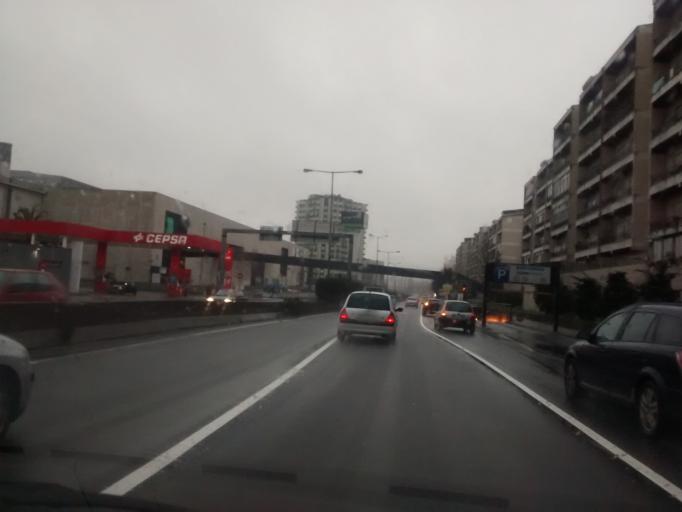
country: PT
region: Braga
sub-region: Braga
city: Braga
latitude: 41.5588
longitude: -8.4075
